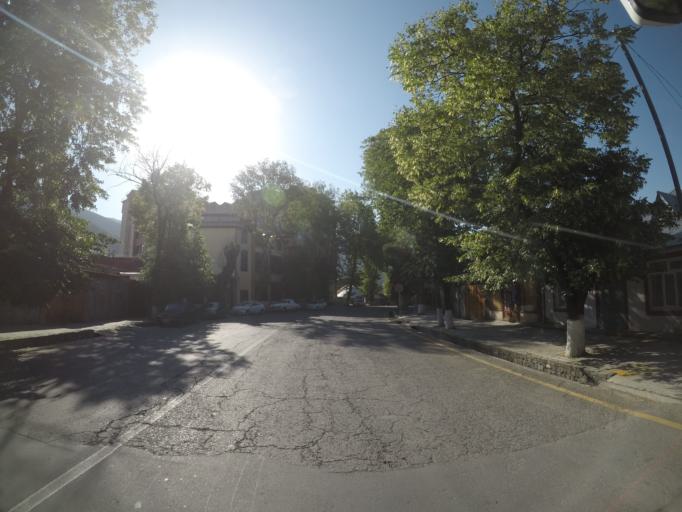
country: AZ
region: Shaki City
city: Sheki
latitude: 41.2054
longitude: 47.1765
